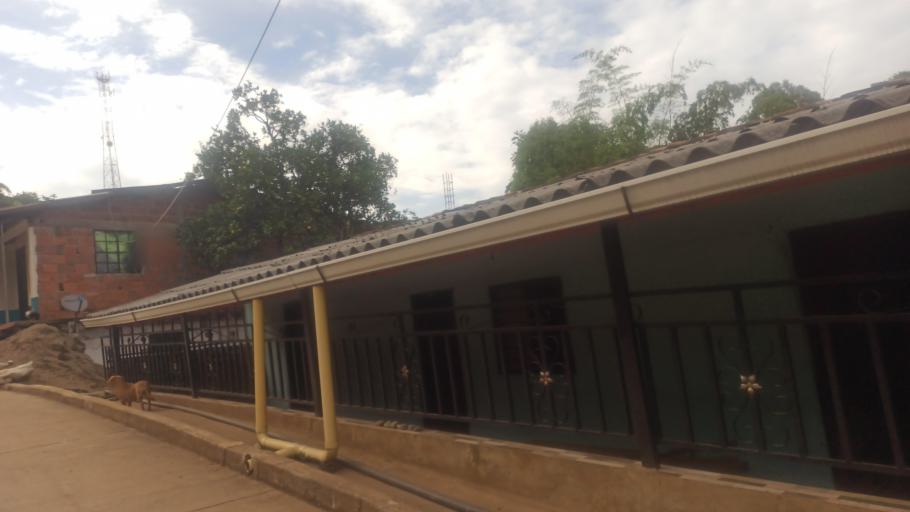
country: CO
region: Valle del Cauca
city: Jamundi
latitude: 3.1860
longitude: -76.6731
